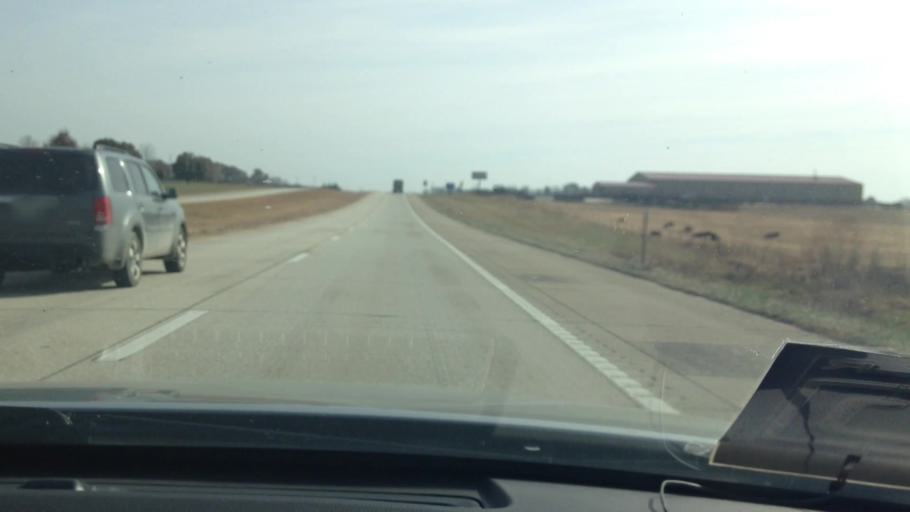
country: US
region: Missouri
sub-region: Henry County
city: Clinton
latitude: 38.4165
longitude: -93.8634
